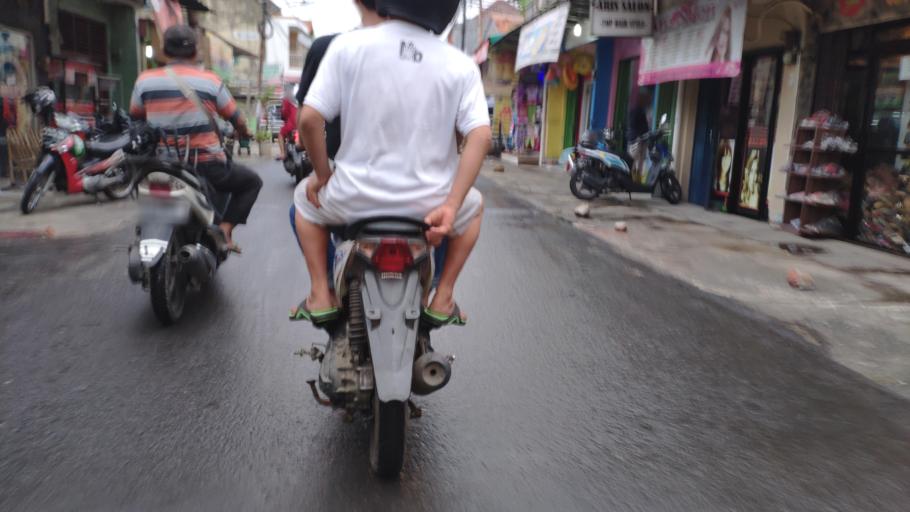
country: ID
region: Jakarta Raya
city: Jakarta
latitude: -6.2115
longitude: 106.8690
